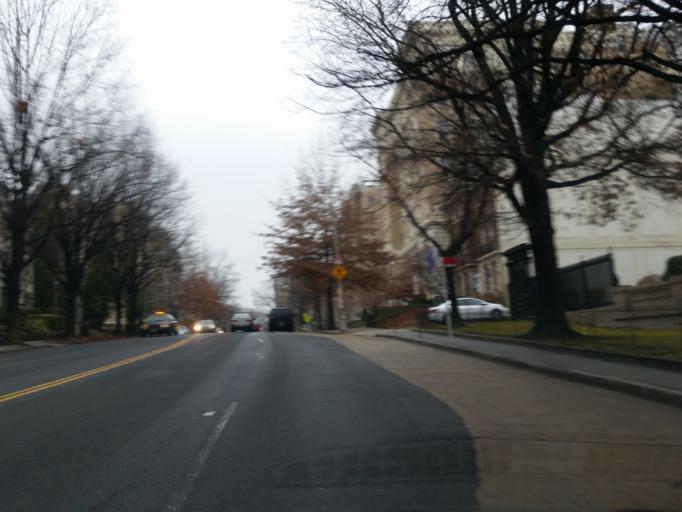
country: US
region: Washington, D.C.
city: Washington, D.C.
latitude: 38.9169
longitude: -77.0467
